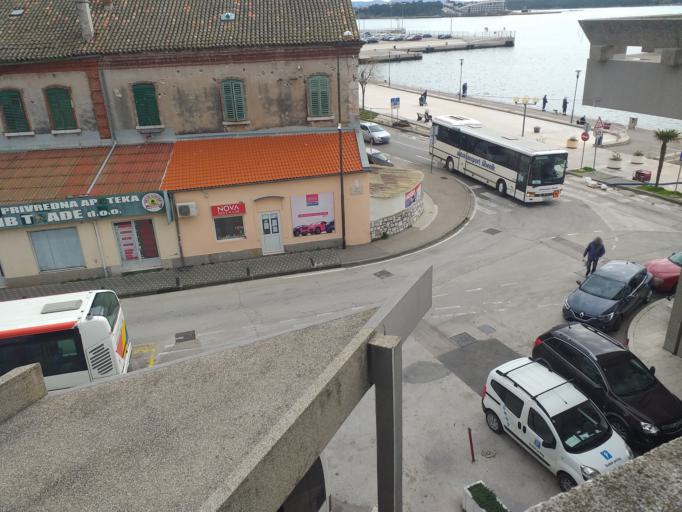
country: HR
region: Sibensko-Kniniska
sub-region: Grad Sibenik
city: Sibenik
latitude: 43.7320
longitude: 15.8932
